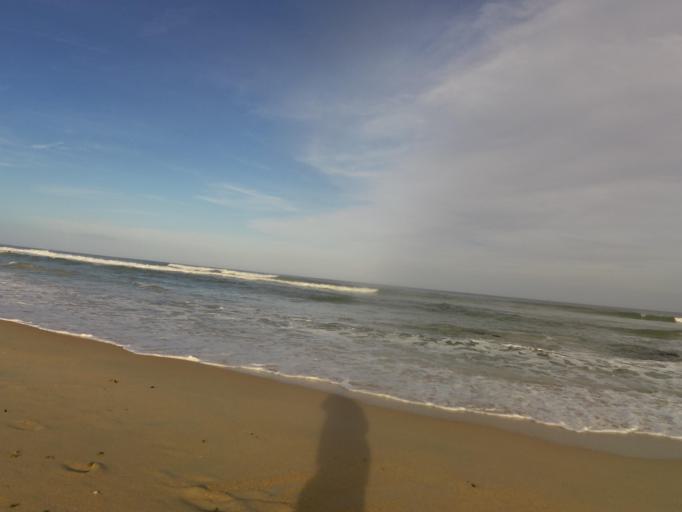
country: US
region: Florida
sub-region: Flagler County
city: Palm Coast
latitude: 29.6158
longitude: -81.1896
